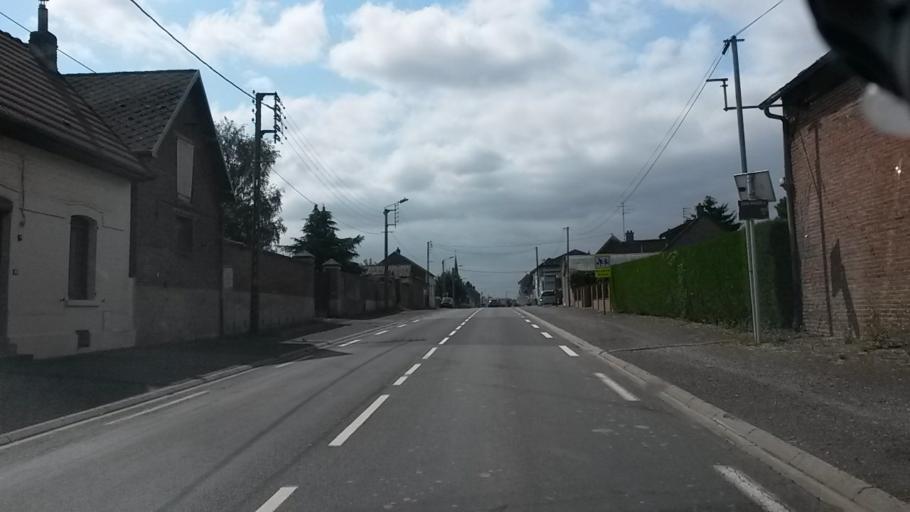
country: FR
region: Nord-Pas-de-Calais
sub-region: Departement du Pas-de-Calais
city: Vaulx-Vraucourt
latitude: 50.1205
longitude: 2.9376
